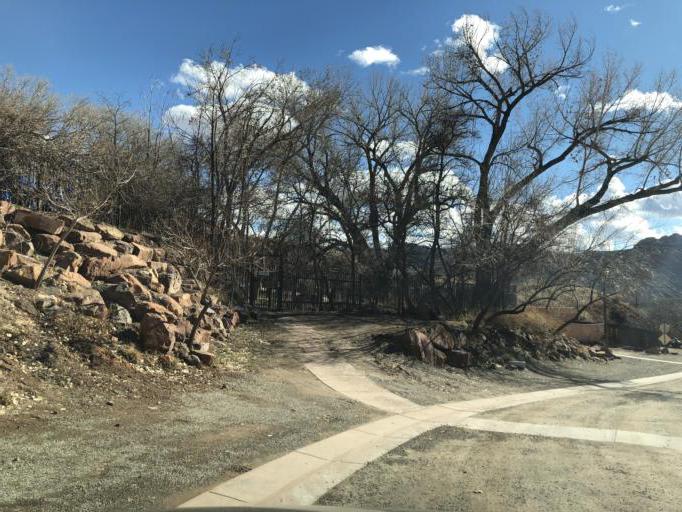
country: US
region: Utah
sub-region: Grand County
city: Moab
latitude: 38.5930
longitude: -109.5632
